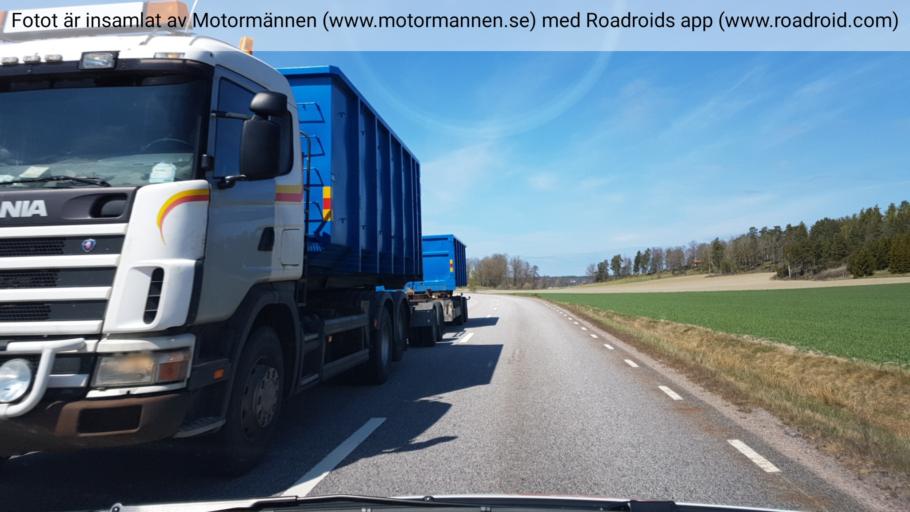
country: SE
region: Kalmar
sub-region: Vasterviks Kommun
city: Forserum
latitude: 57.9383
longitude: 16.4996
